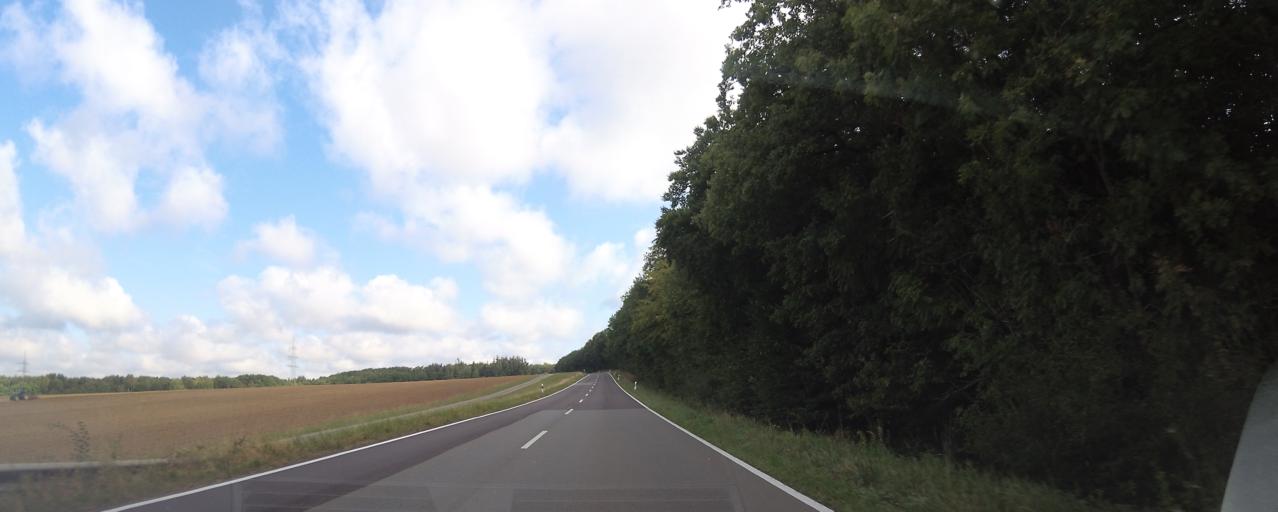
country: DE
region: Rheinland-Pfalz
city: Zemmer
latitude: 49.9004
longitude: 6.7076
